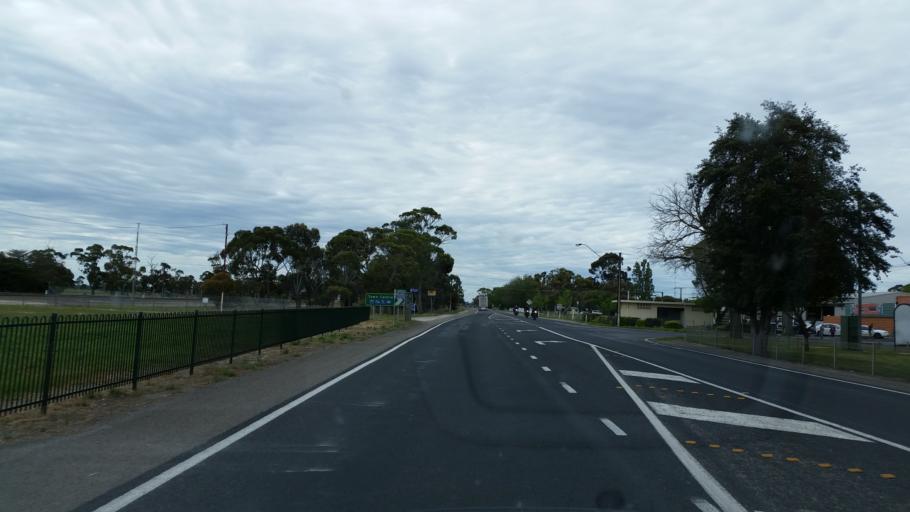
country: AU
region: South Australia
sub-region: Tatiara
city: Keith
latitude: -36.0976
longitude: 140.3546
